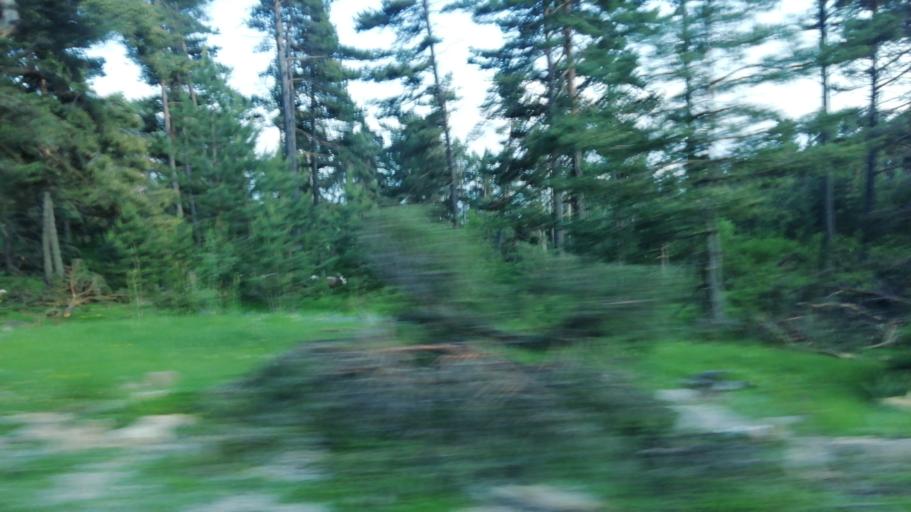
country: TR
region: Karabuk
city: Eskipazar
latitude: 41.0453
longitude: 32.5534
